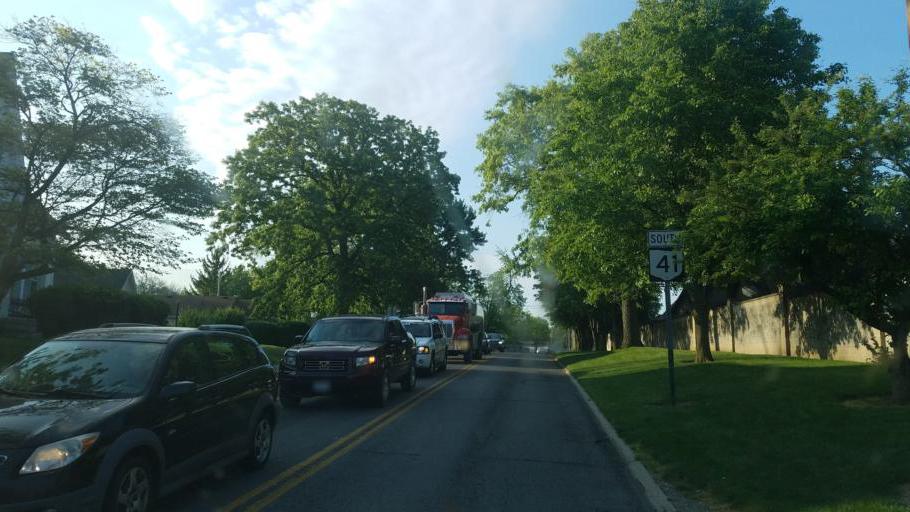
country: US
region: Ohio
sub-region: Fayette County
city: Washington Court House
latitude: 39.5324
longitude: -83.4443
